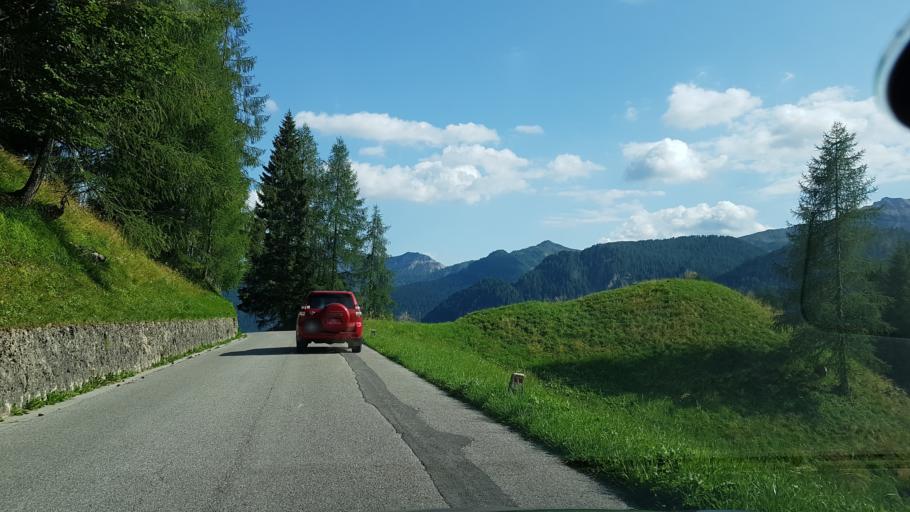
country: IT
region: Friuli Venezia Giulia
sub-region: Provincia di Udine
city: Sauris di Sotto
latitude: 46.4736
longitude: 12.6696
